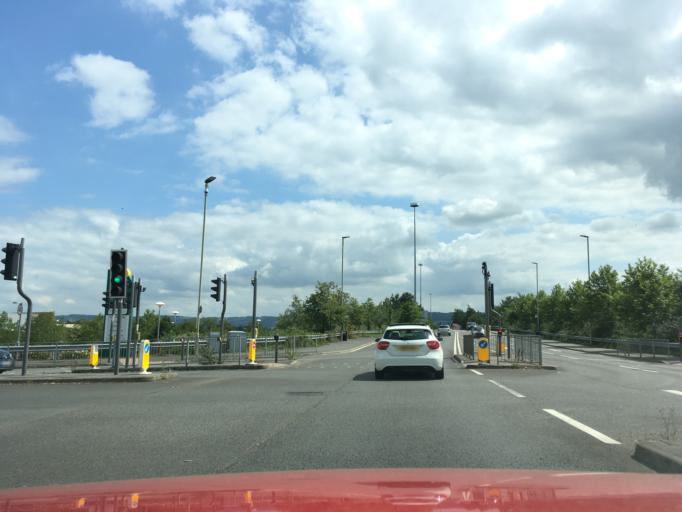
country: GB
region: England
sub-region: Gloucestershire
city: Gloucester
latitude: 51.8603
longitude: -2.2253
